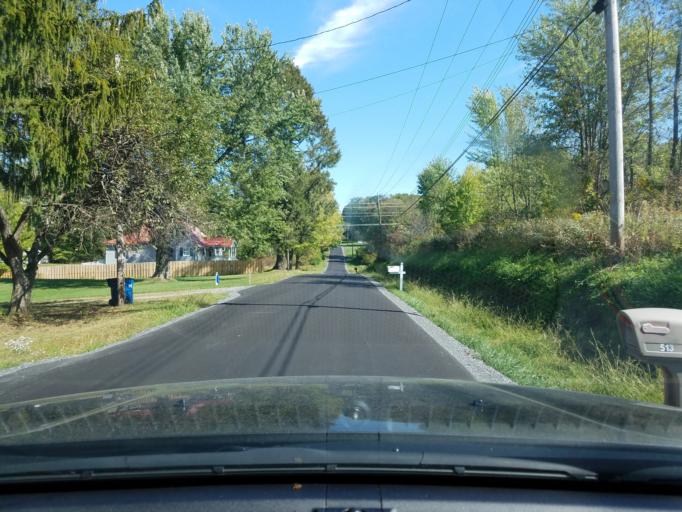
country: US
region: Pennsylvania
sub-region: Lawrence County
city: Ellwood City
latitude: 40.9357
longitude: -80.3000
